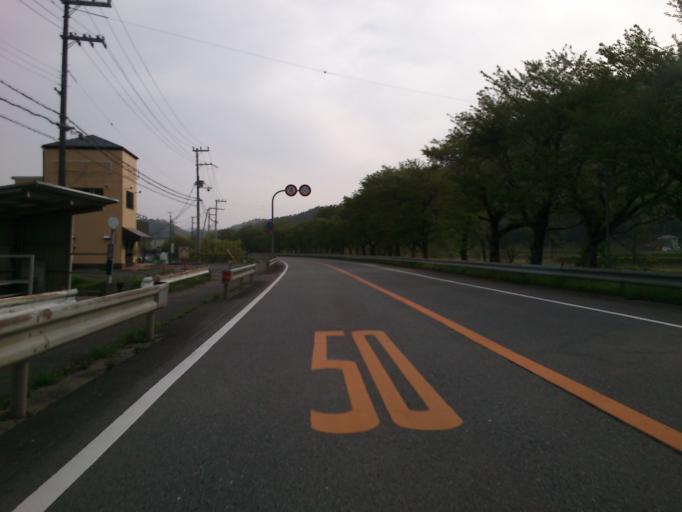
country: JP
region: Hyogo
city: Sasayama
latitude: 35.1077
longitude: 135.3201
